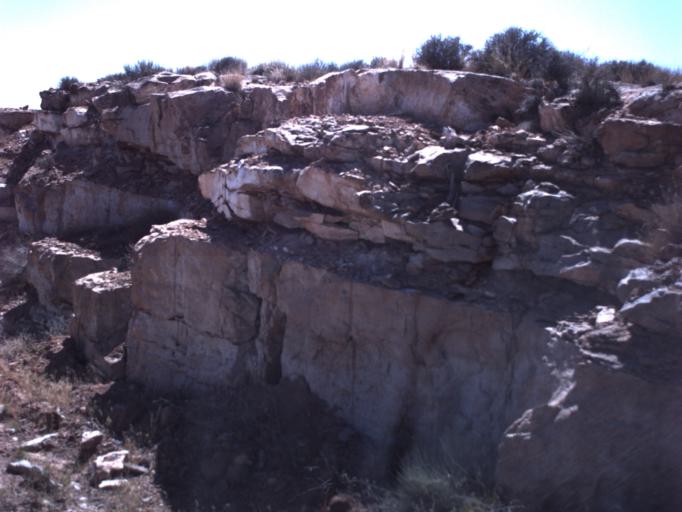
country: US
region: Arizona
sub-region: Navajo County
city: Kayenta
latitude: 37.1933
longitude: -109.9108
